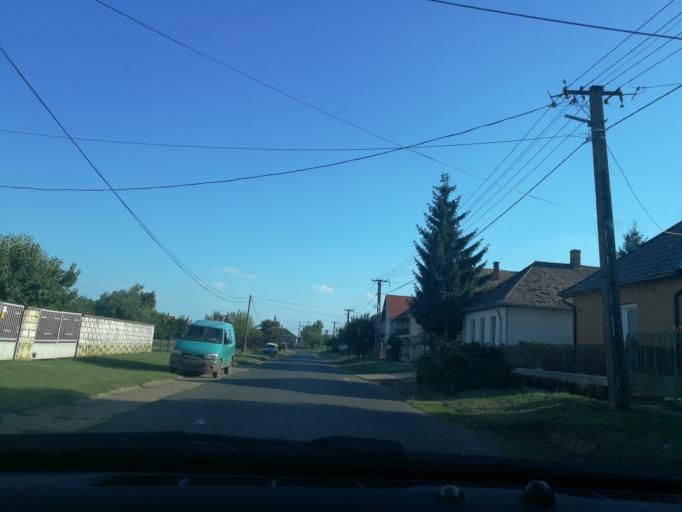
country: HU
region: Szabolcs-Szatmar-Bereg
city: Tiszabercel
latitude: 48.1673
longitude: 21.5643
